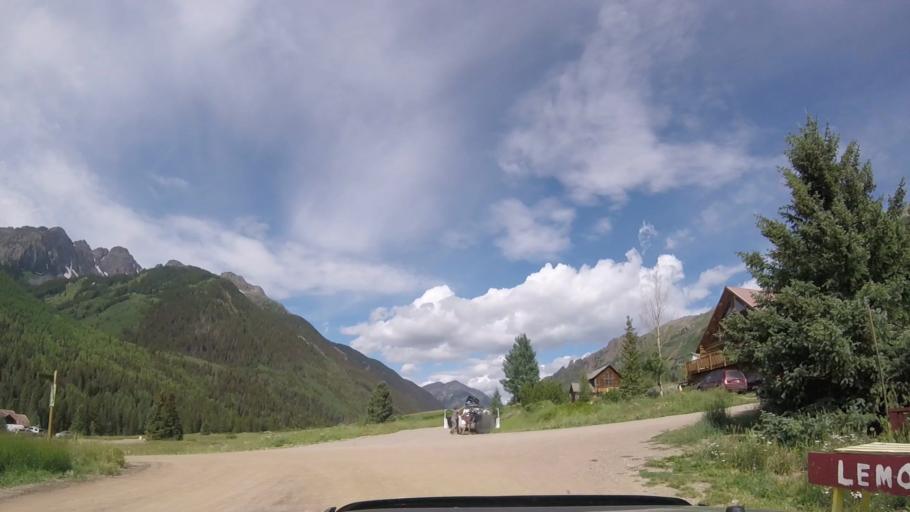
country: US
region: Colorado
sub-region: San Miguel County
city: Mountain Village
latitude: 37.8564
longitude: -107.8251
